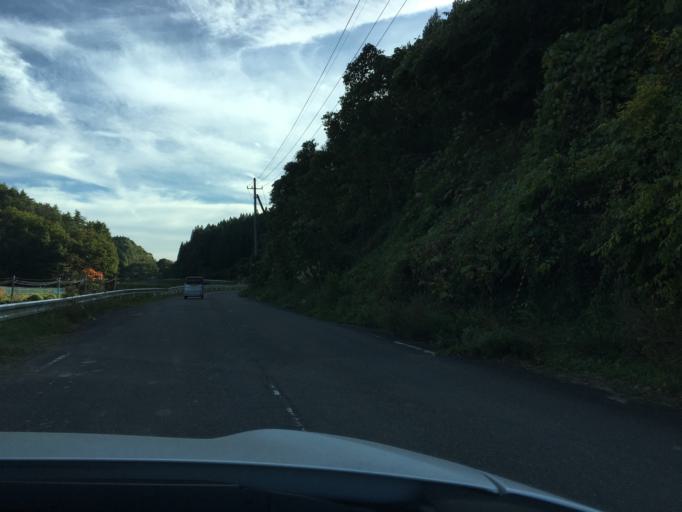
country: JP
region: Fukushima
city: Funehikimachi-funehiki
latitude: 37.2732
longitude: 140.6070
